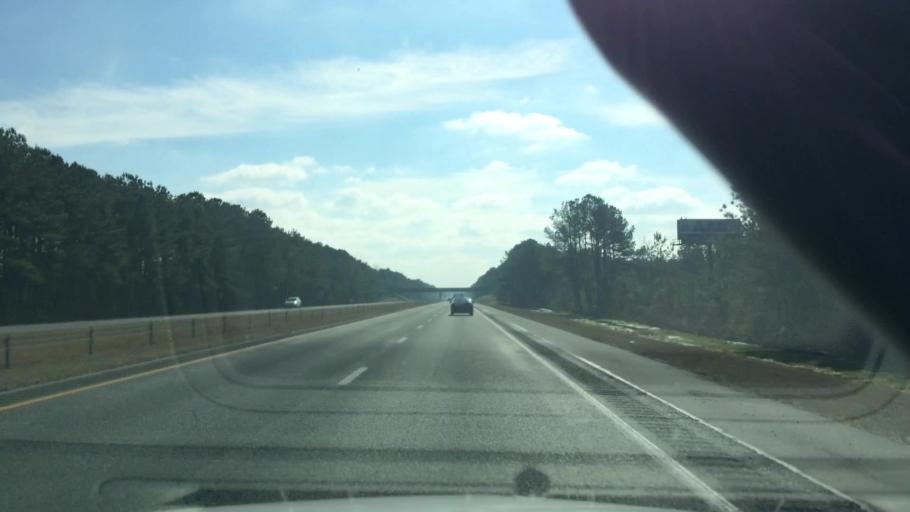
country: US
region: North Carolina
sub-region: Duplin County
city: Wallace
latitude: 34.7367
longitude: -77.9447
